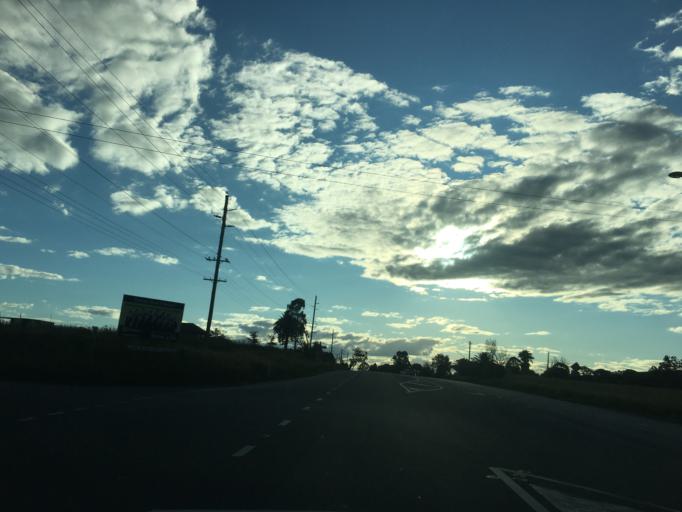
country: AU
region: New South Wales
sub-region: Liverpool
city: Bringelly
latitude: -33.8752
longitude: 150.7636
